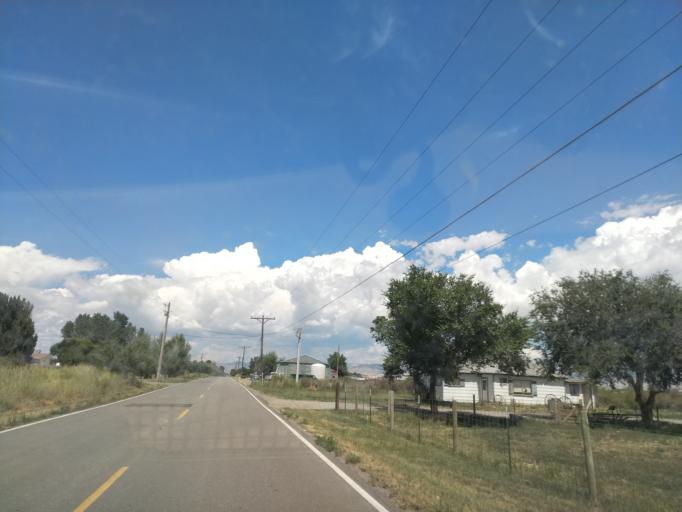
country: US
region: Colorado
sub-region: Mesa County
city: Redlands
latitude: 39.1274
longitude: -108.6640
